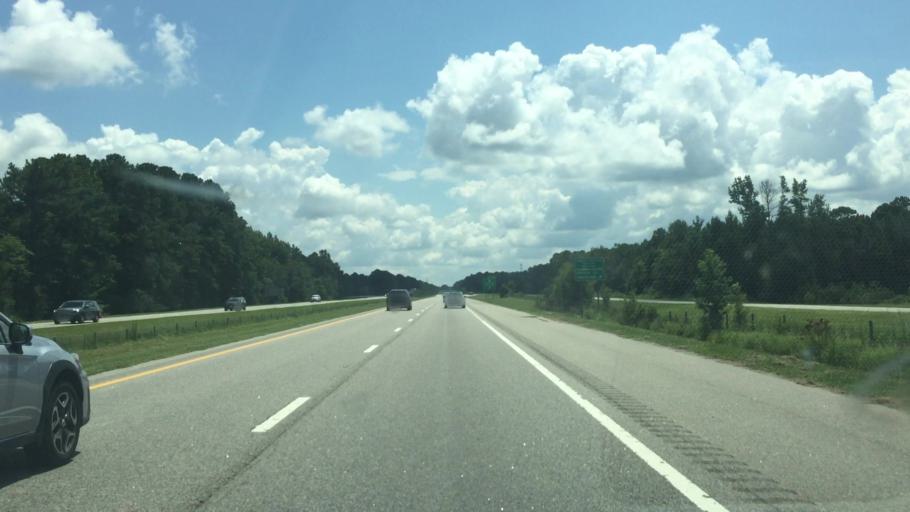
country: US
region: North Carolina
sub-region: Robeson County
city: Lumberton
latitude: 34.5837
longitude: -79.0559
